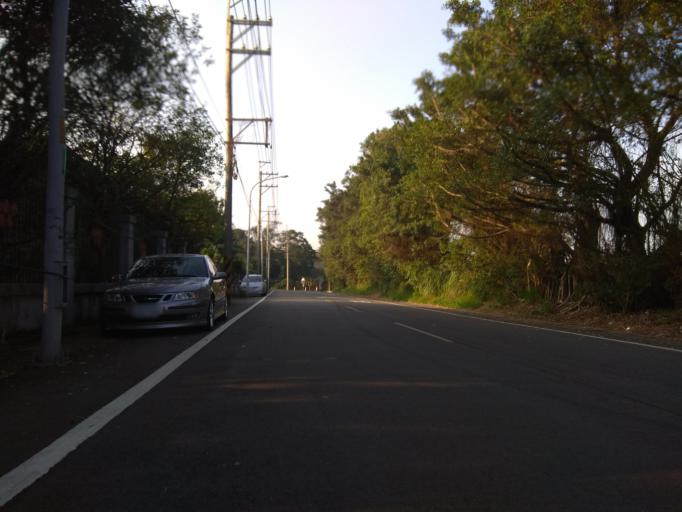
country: TW
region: Taiwan
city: Daxi
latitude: 24.9290
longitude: 121.1797
